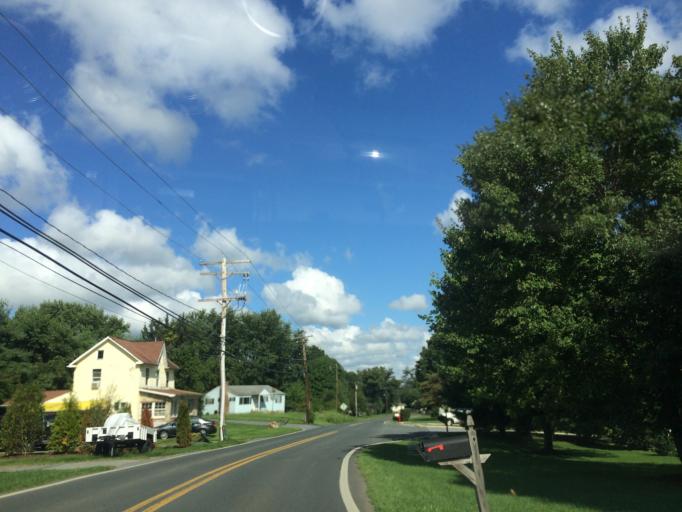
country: US
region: Maryland
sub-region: Carroll County
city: Eldersburg
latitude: 39.4185
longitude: -76.9615
